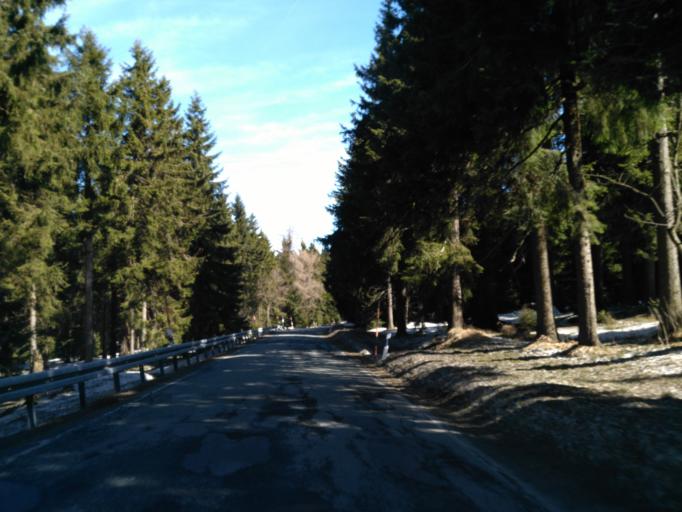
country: DE
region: Saxony
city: Kurort Oberwiesenthal
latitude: 50.4211
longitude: 12.9299
